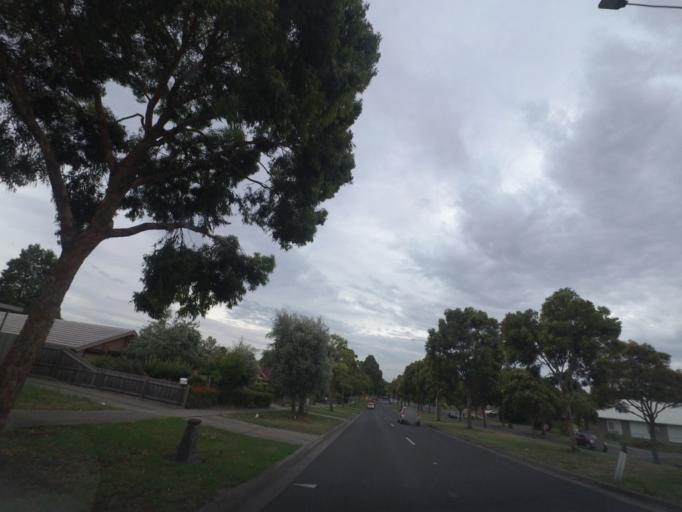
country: AU
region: Victoria
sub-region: Whittlesea
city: Mill Park
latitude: -37.6608
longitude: 145.0549
